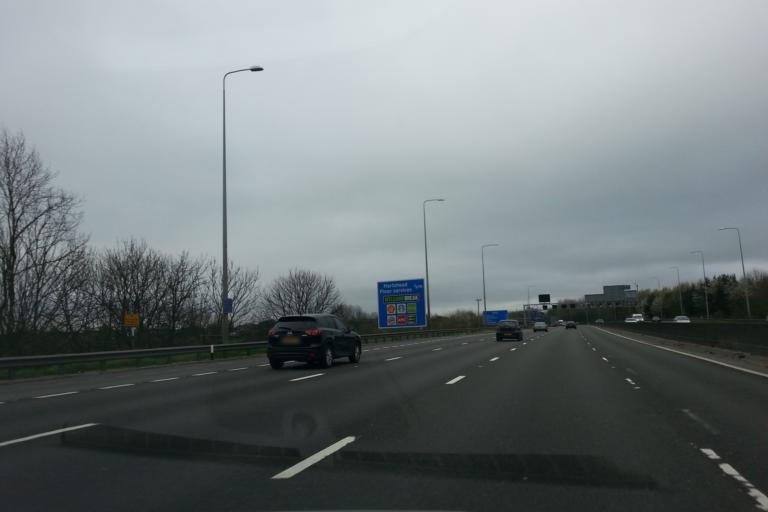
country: GB
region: England
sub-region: Kirklees
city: Cleckheaton
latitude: 53.7237
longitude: -1.7384
